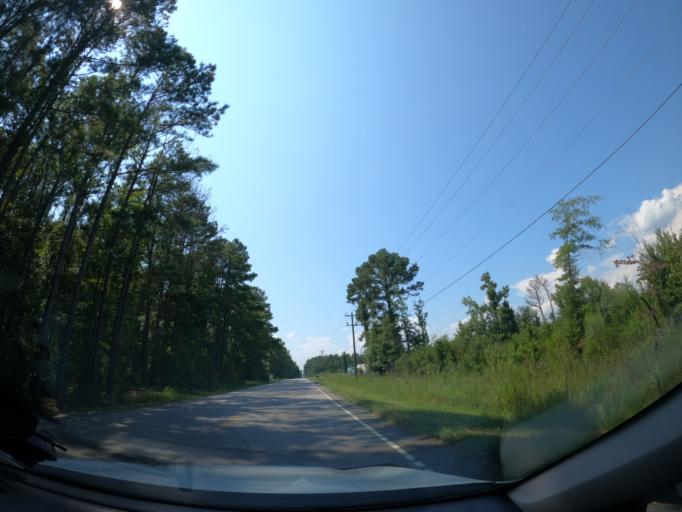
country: US
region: South Carolina
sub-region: Richland County
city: Hopkins
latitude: 33.9053
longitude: -80.9303
